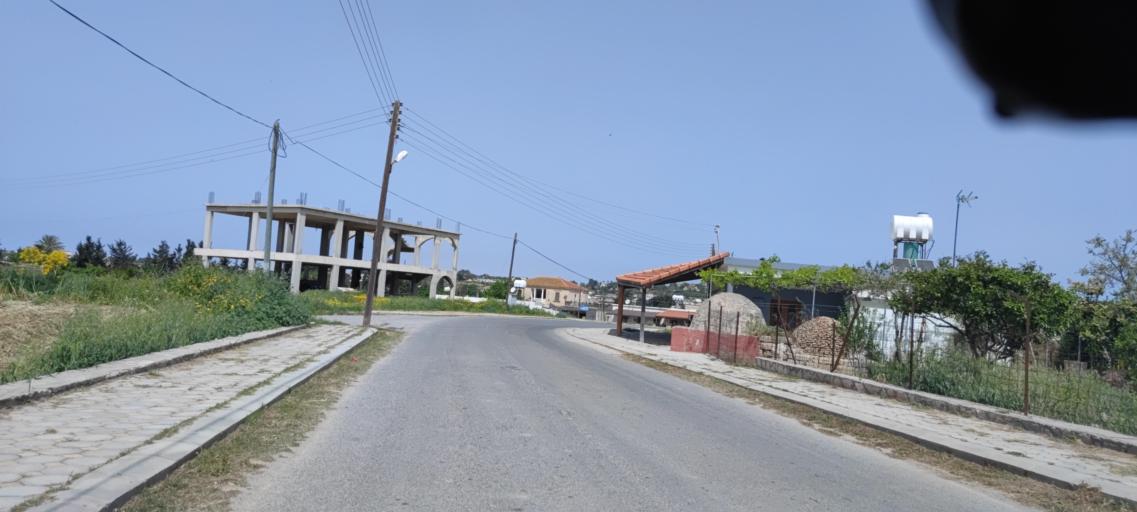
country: CY
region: Ammochostos
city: Rizokarpaso
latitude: 35.5923
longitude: 34.3859
